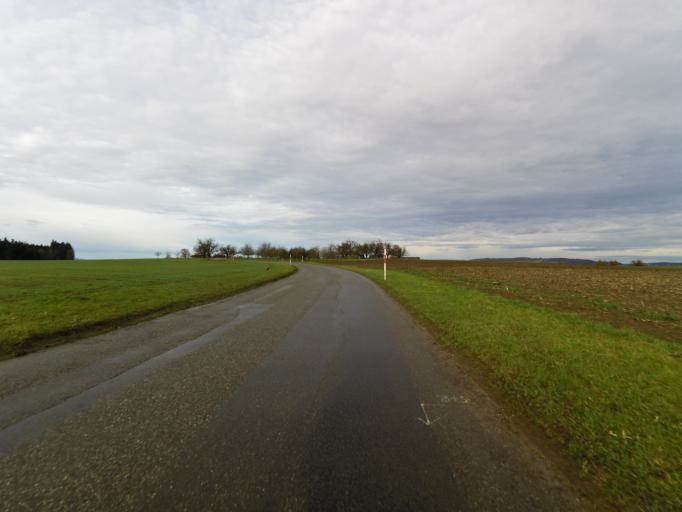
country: CH
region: Thurgau
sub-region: Frauenfeld District
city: Thundorf
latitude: 47.5583
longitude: 8.9336
